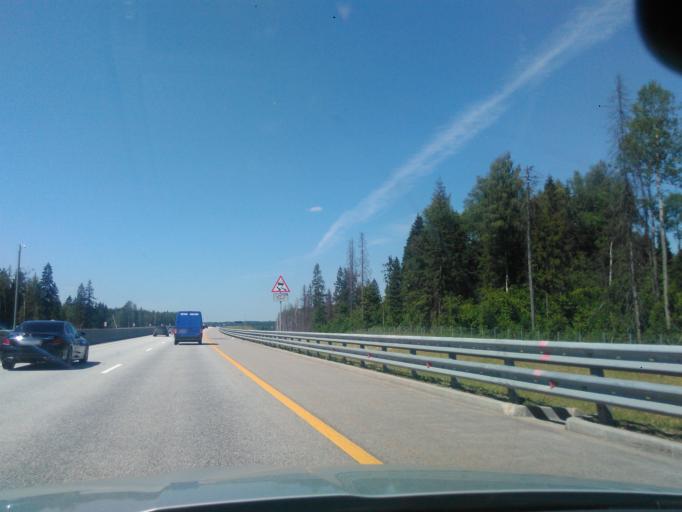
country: RU
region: Moskovskaya
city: Mendeleyevo
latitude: 56.0763
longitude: 37.2135
